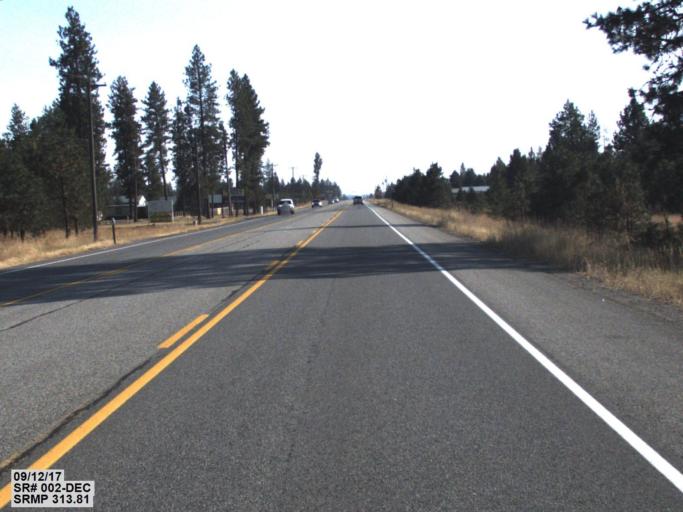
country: US
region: Washington
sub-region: Spokane County
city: Deer Park
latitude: 48.0233
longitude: -117.3497
